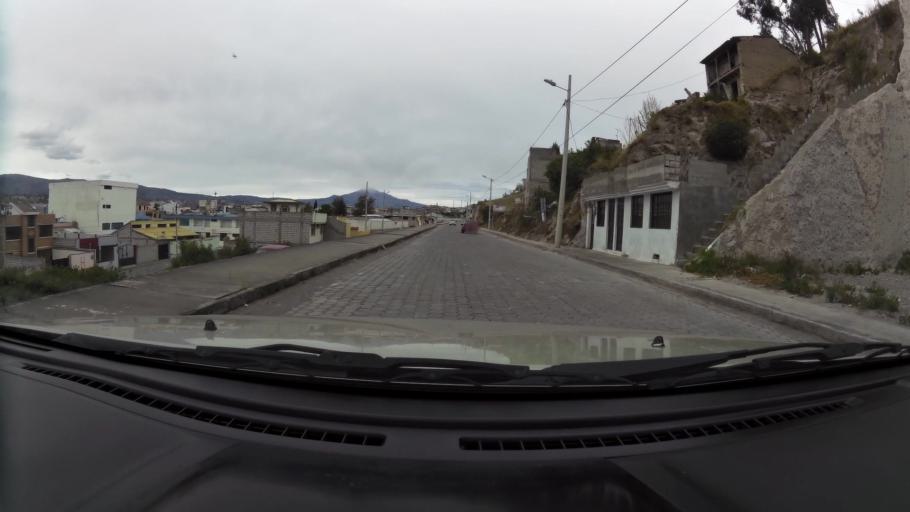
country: EC
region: Cotopaxi
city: Latacunga
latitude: -0.9405
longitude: -78.6090
